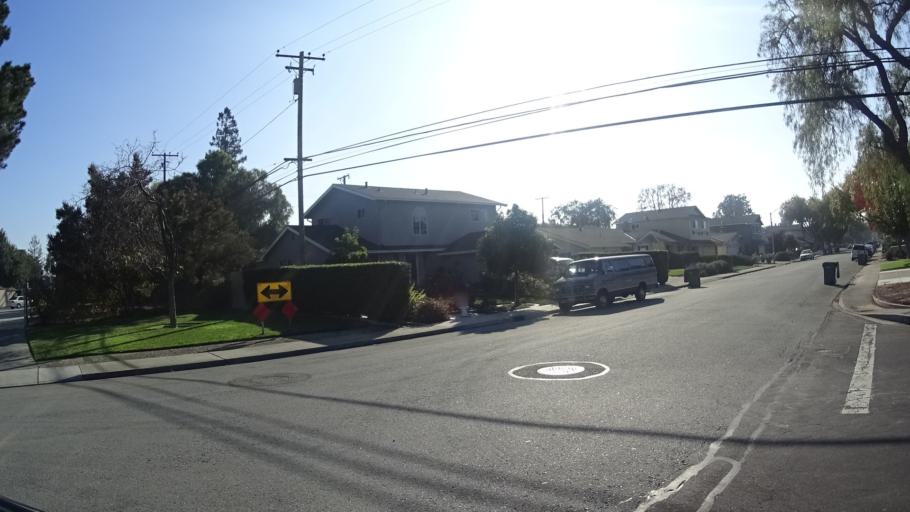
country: US
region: California
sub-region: Santa Clara County
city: Santa Clara
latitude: 37.3585
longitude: -121.9784
